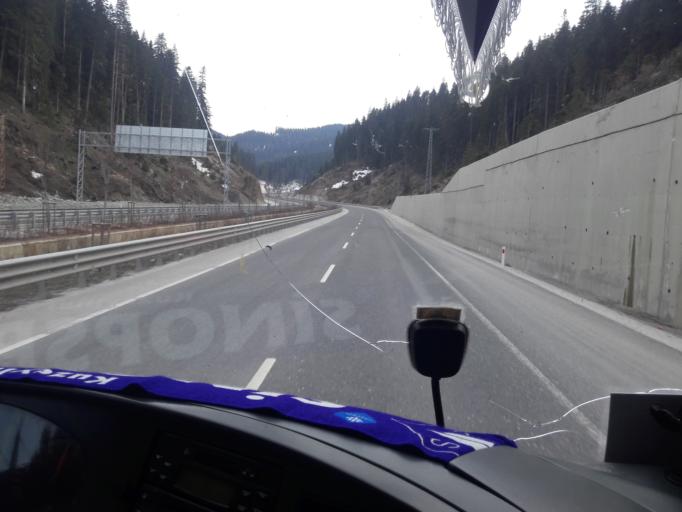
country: TR
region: Kastamonu
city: Kuzyaka
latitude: 41.0972
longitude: 33.7496
